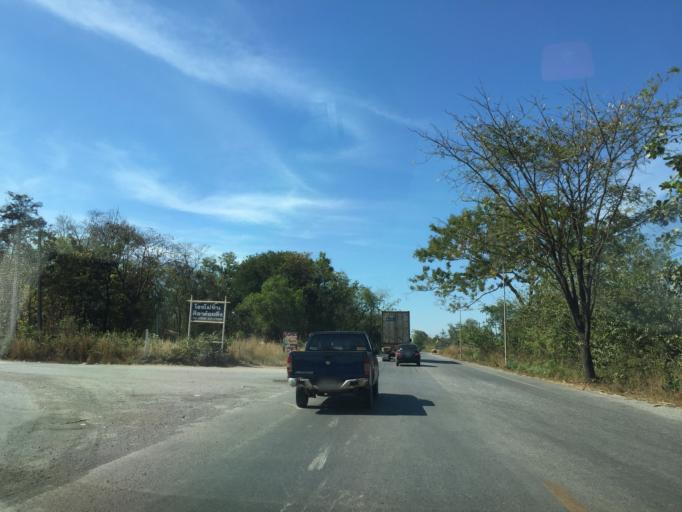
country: TH
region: Changwat Nong Bua Lamphu
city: Na Klang
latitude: 17.3128
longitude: 102.1695
